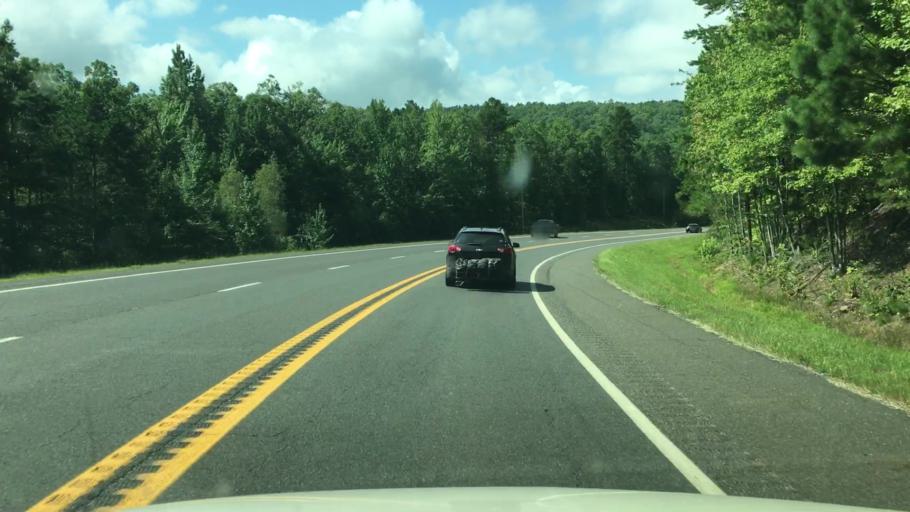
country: US
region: Arkansas
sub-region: Garland County
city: Lake Hamilton
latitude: 34.3655
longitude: -93.1617
